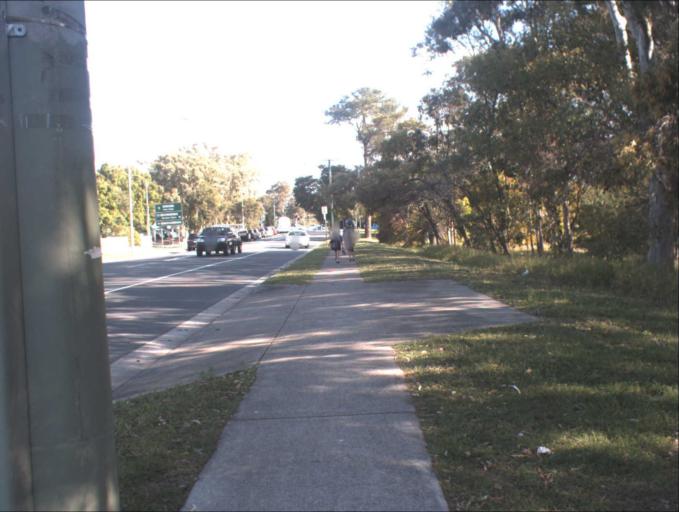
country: AU
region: Queensland
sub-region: Logan
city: Logan City
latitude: -27.6787
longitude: 153.0890
